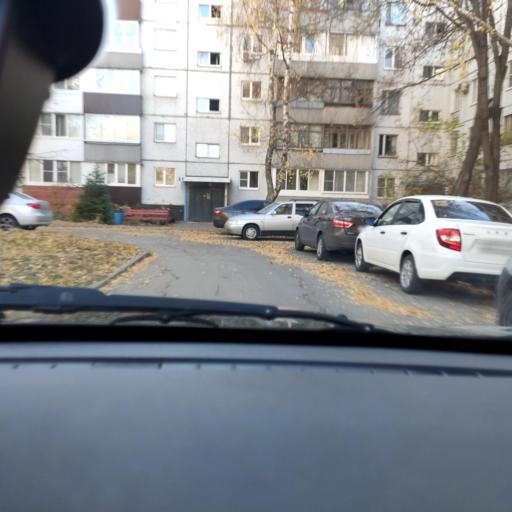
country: RU
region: Samara
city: Tol'yatti
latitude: 53.5377
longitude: 49.2700
